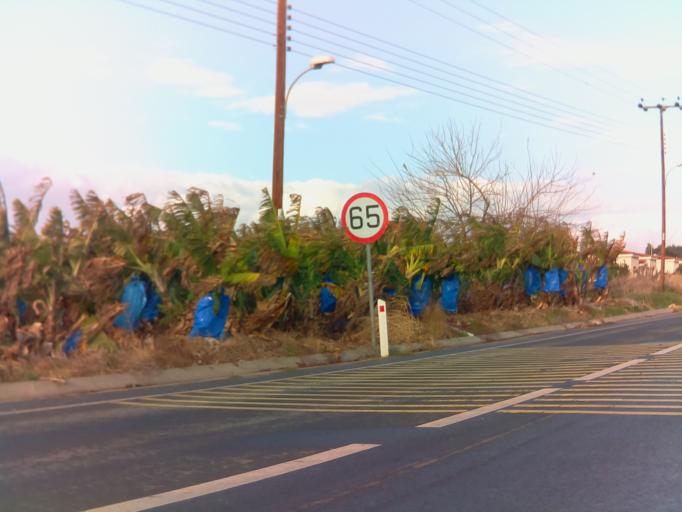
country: CY
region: Pafos
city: Pegeia
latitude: 34.8587
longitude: 32.3756
